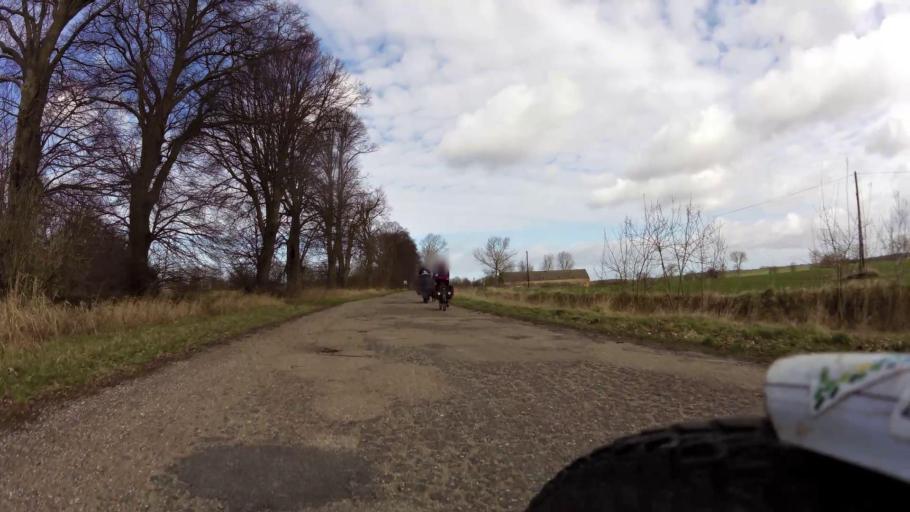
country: PL
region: West Pomeranian Voivodeship
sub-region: Powiat kamienski
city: Kamien Pomorski
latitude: 53.9902
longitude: 14.7680
